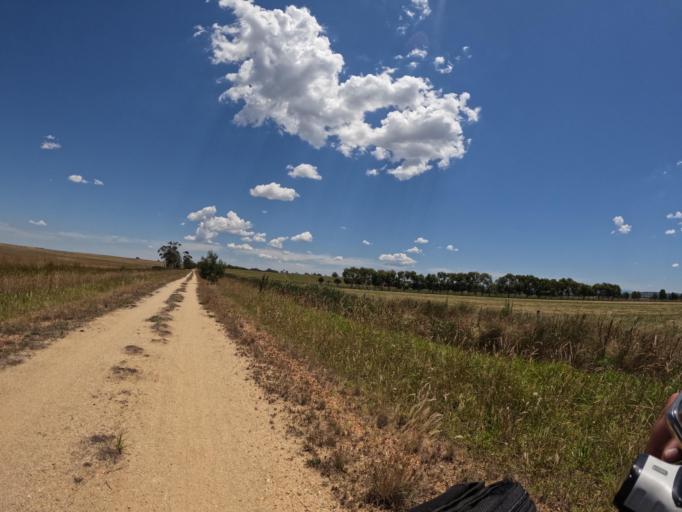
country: AU
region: Victoria
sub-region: Wellington
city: Heyfield
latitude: -37.9752
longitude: 146.8630
